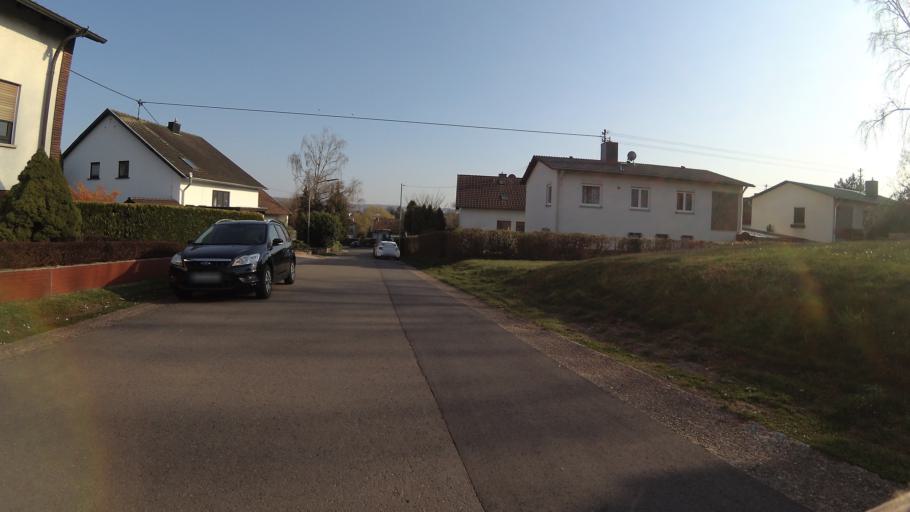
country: DE
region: Saarland
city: Heusweiler
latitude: 49.3448
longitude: 6.9299
